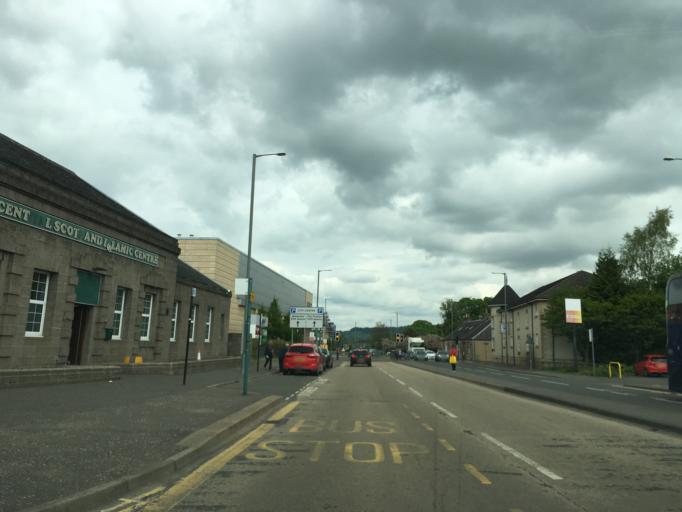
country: GB
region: Scotland
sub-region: Stirling
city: Stirling
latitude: 56.1132
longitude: -3.9327
